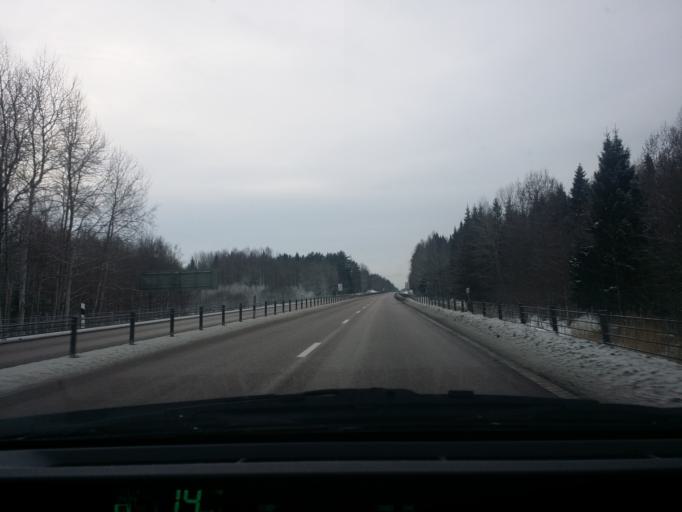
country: SE
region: Vaestra Goetaland
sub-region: Mariestads Kommun
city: Mariestad
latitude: 58.6125
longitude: 13.8055
